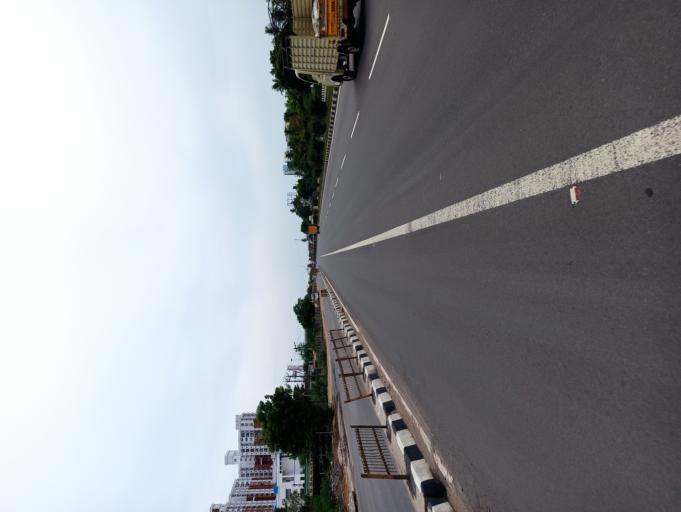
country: IN
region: Tamil Nadu
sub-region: Kancheepuram
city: Poonamalle
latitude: 13.0570
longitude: 80.1074
